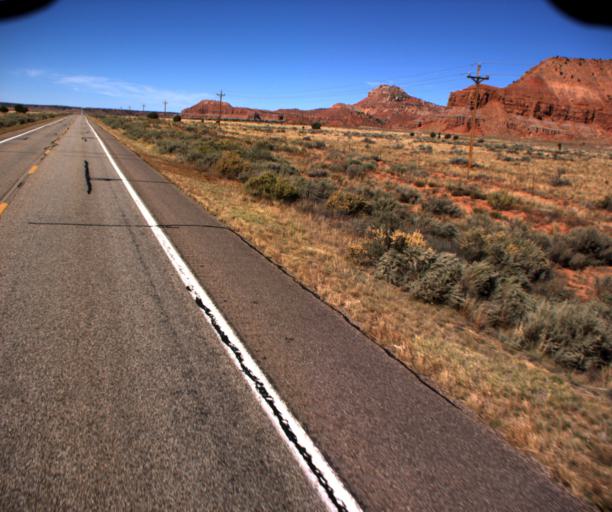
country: US
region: Arizona
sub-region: Mohave County
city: Colorado City
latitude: 36.8606
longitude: -112.8173
